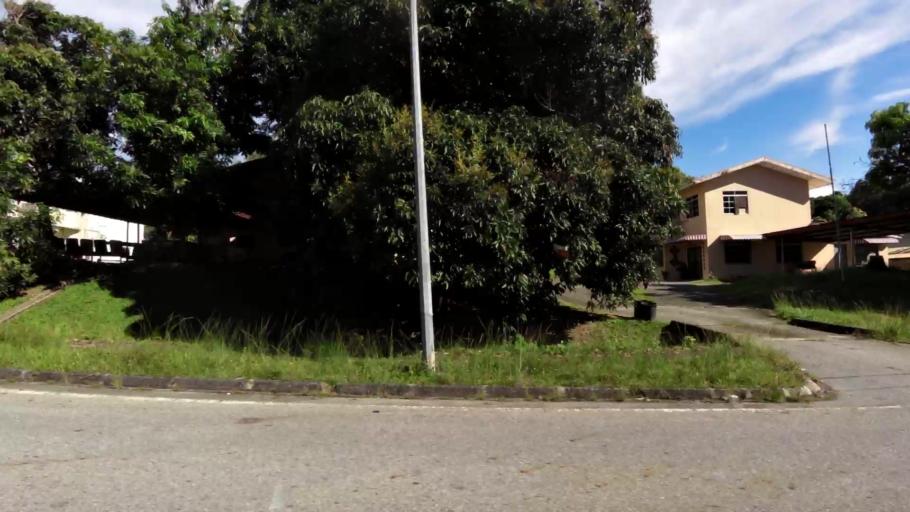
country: BN
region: Brunei and Muara
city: Bandar Seri Begawan
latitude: 4.9771
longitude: 114.9603
